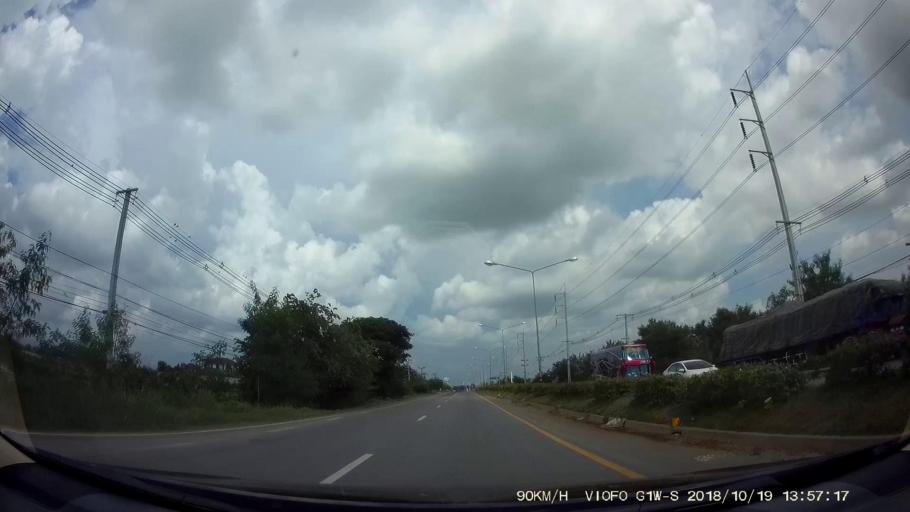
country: TH
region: Chaiyaphum
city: Chaiyaphum
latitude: 15.7891
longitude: 102.0397
